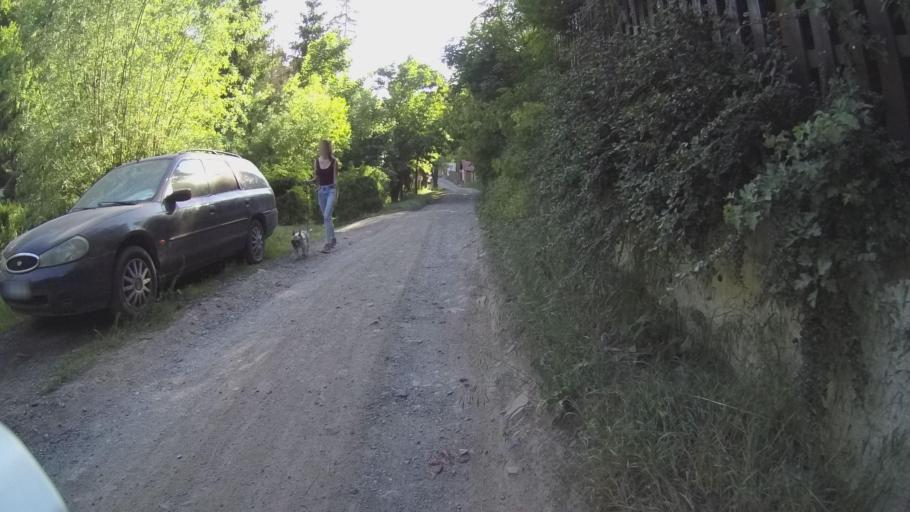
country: CZ
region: Central Bohemia
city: Roztoky
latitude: 50.1495
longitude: 14.4201
